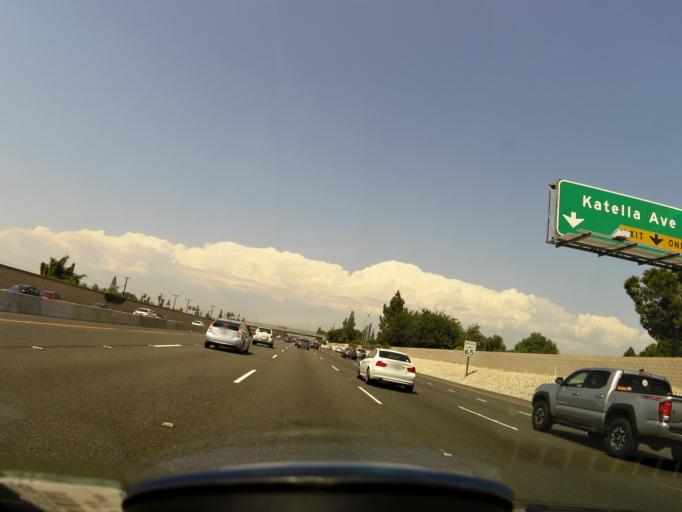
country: US
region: California
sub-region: Orange County
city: Villa Park
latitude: 33.7989
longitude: -117.8312
